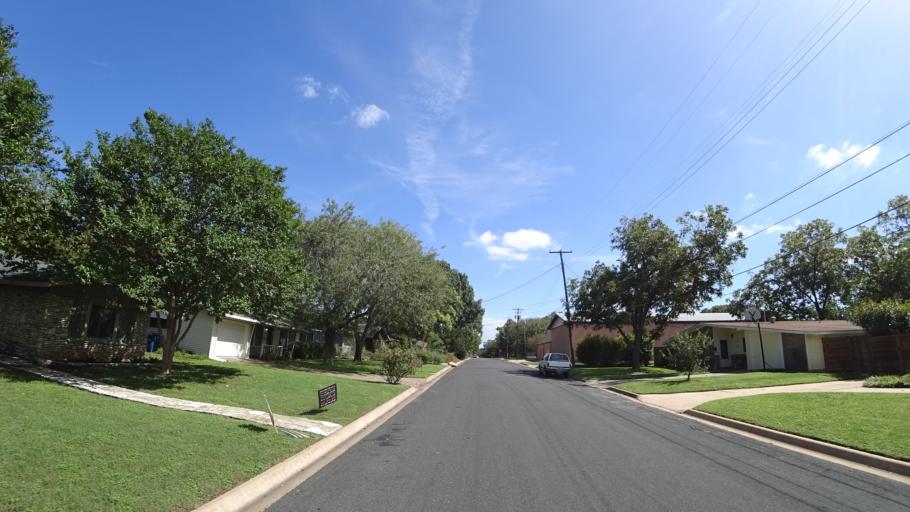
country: US
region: Texas
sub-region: Travis County
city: Austin
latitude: 30.3403
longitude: -97.7280
